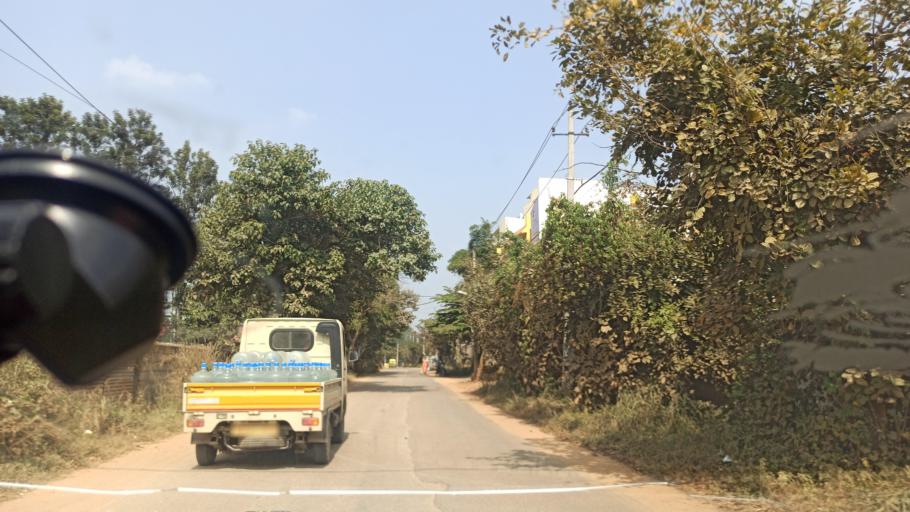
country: IN
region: Karnataka
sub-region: Bangalore Urban
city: Yelahanka
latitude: 13.0954
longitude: 77.6185
